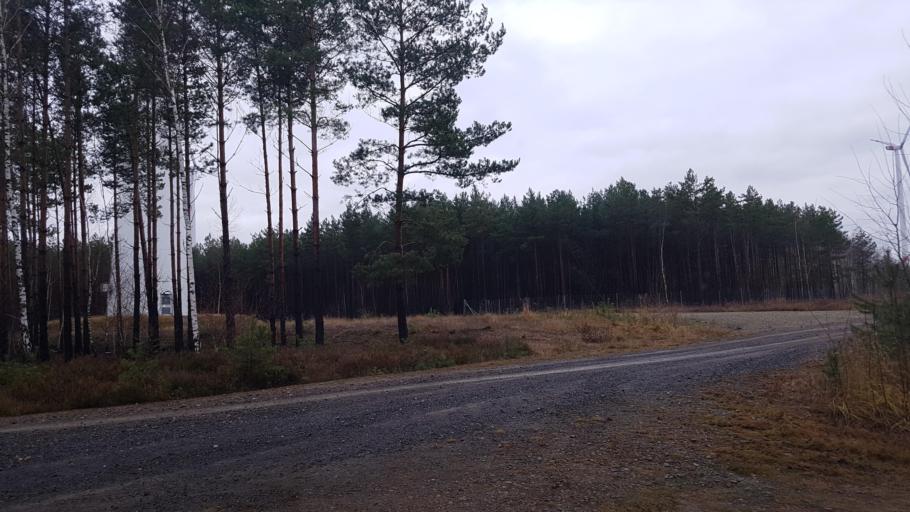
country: DE
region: Brandenburg
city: Grossraschen
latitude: 51.6248
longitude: 13.9699
